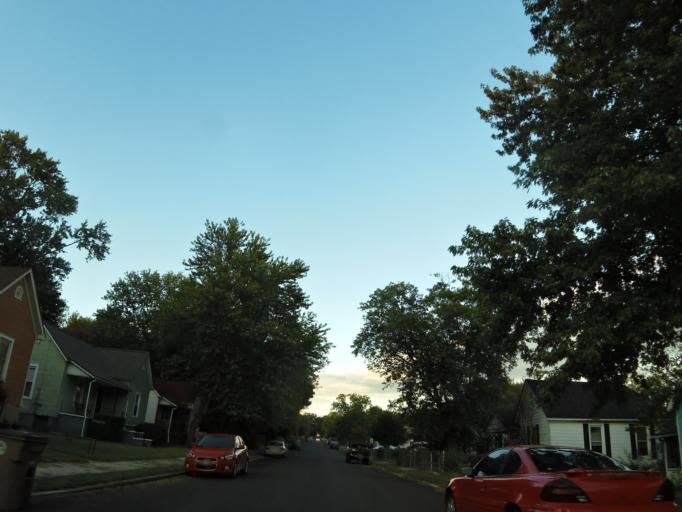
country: US
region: Tennessee
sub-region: Knox County
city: Knoxville
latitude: 35.9868
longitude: -83.9330
